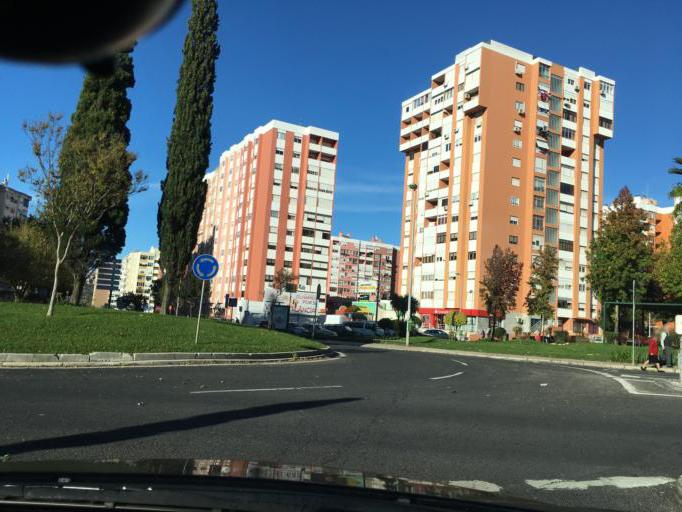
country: PT
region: Lisbon
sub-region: Odivelas
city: Pontinha
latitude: 38.7635
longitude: -9.2072
